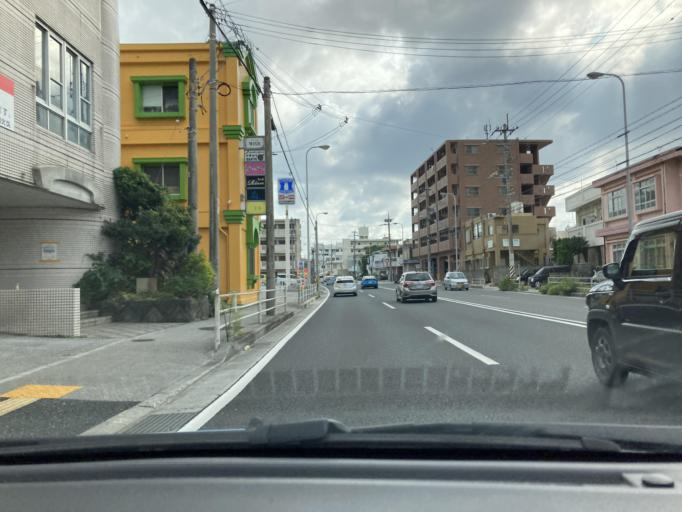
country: JP
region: Okinawa
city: Ginowan
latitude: 26.2073
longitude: 127.7570
